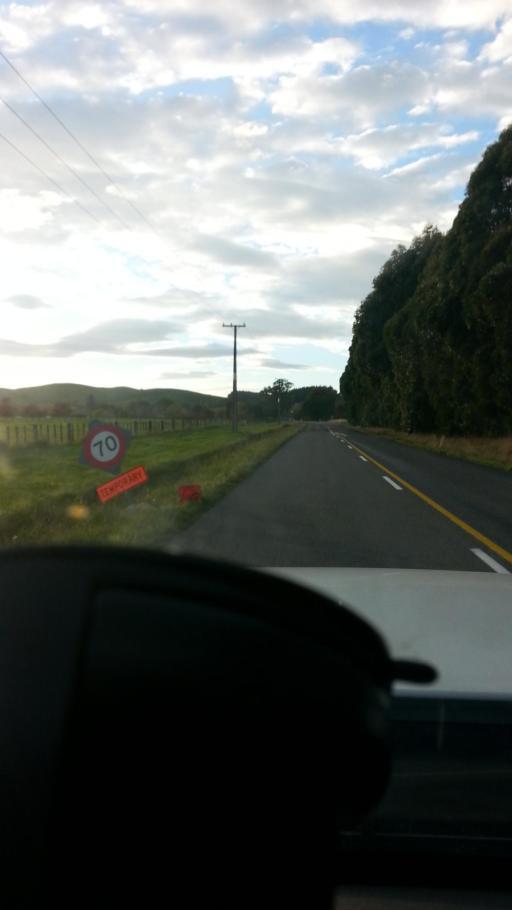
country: NZ
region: Wellington
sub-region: Masterton District
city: Masterton
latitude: -40.9647
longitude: 175.7382
